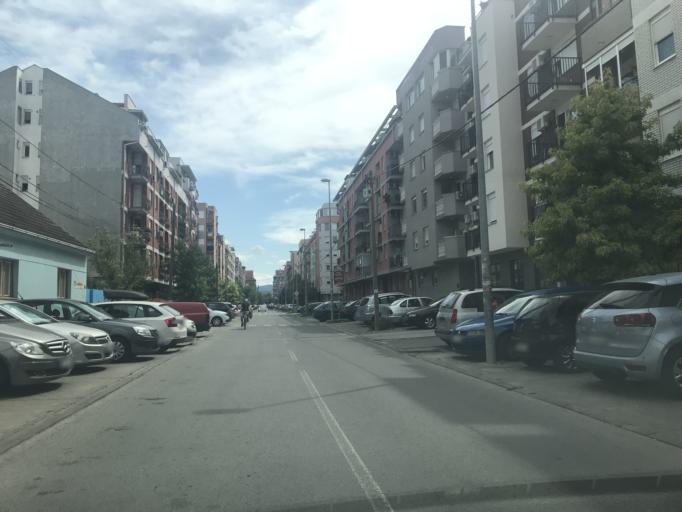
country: RS
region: Autonomna Pokrajina Vojvodina
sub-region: Juznobacki Okrug
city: Novi Sad
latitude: 45.2594
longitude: 19.8120
